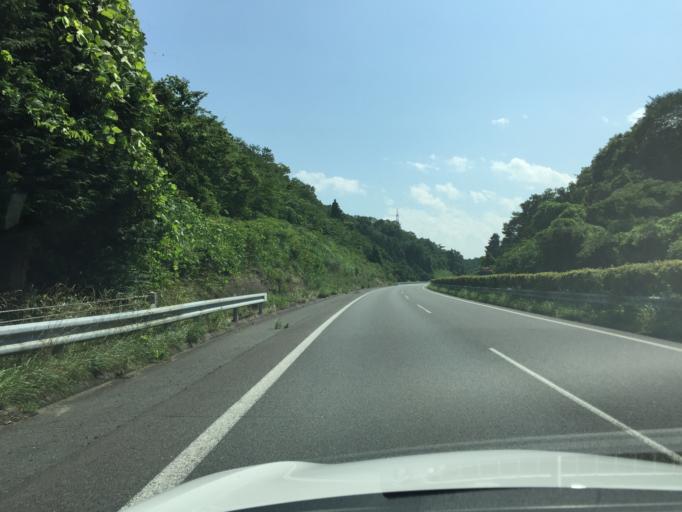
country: JP
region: Fukushima
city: Iwaki
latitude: 36.9721
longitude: 140.7929
